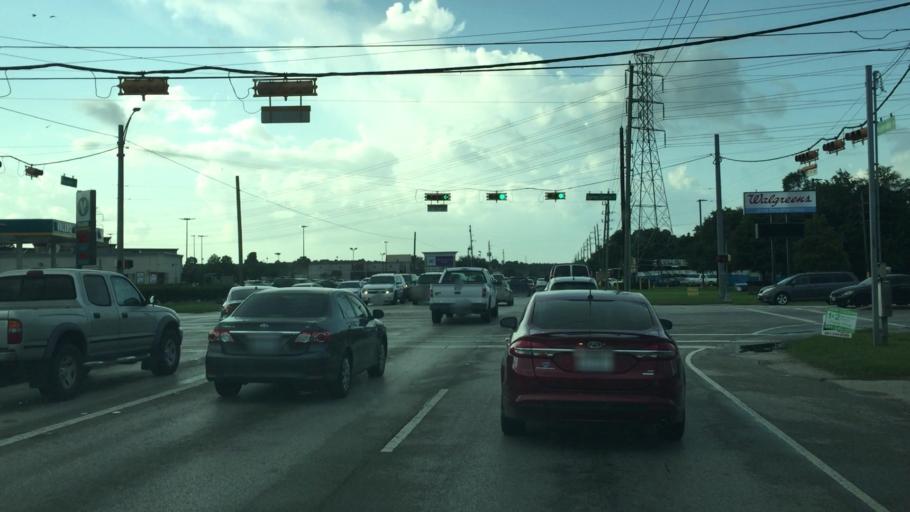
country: US
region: Texas
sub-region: Harris County
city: Spring
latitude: 30.0503
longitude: -95.4926
